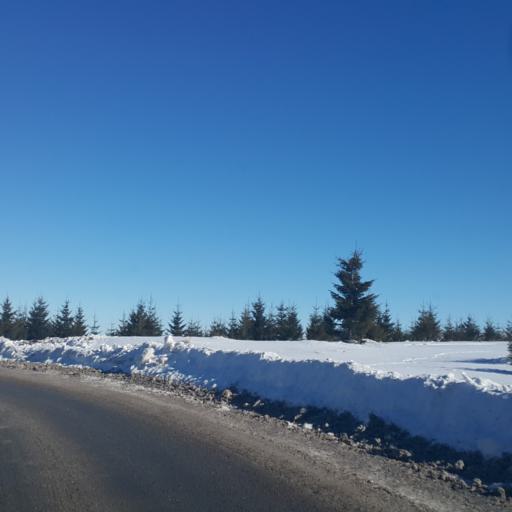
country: XK
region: Mitrovica
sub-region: Komuna e Leposaviqit
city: Leposaviq
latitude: 43.3269
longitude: 20.8524
